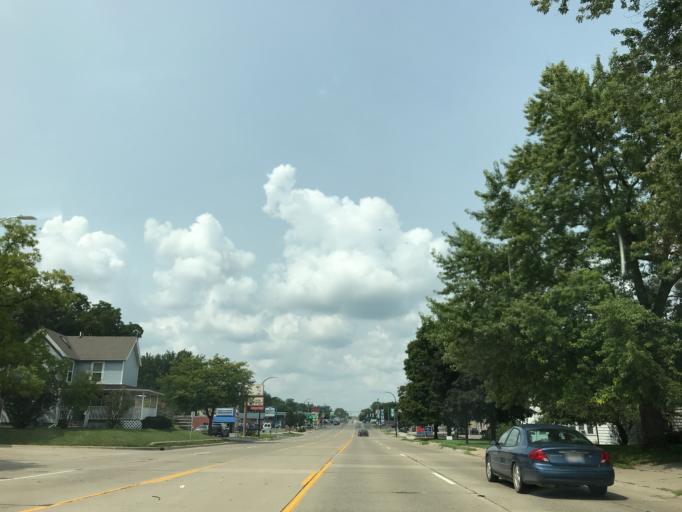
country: US
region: Michigan
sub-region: Washtenaw County
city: Ypsilanti
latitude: 42.2469
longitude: -83.6335
